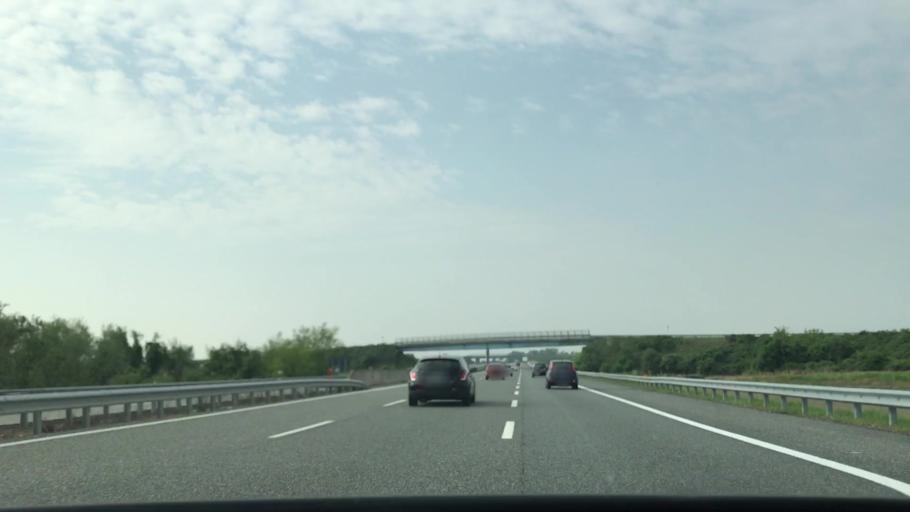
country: IT
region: Piedmont
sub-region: Provincia di Vercelli
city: Prarolo
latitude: 45.2717
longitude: 8.4698
